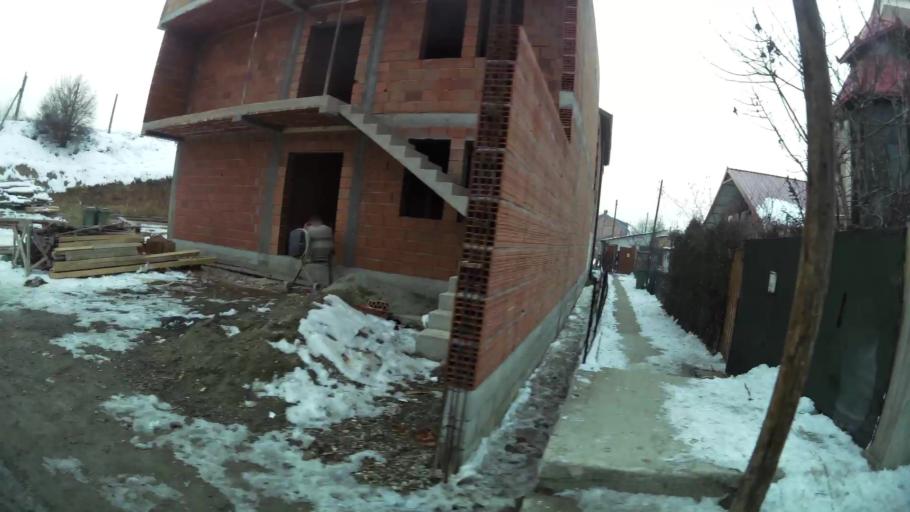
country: MK
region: Suto Orizari
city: Suto Orizare
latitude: 42.0279
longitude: 21.4310
